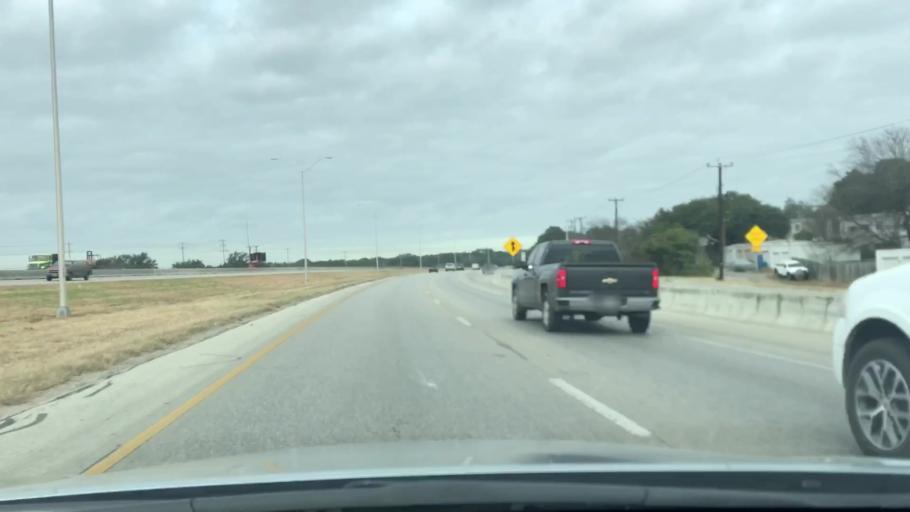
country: US
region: Texas
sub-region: Bexar County
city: Live Oak
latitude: 29.5479
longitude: -98.3171
